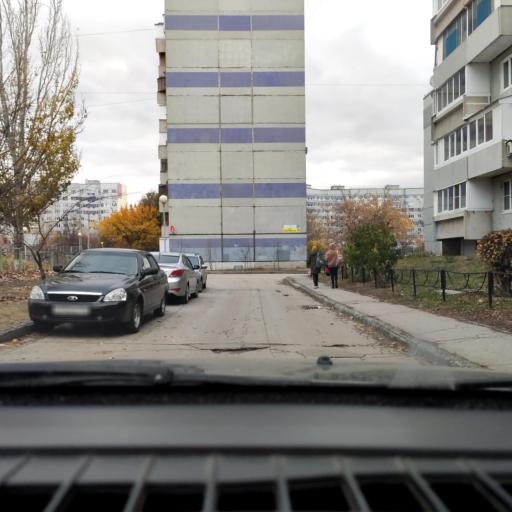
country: RU
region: Samara
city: Tol'yatti
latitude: 53.5391
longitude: 49.3342
